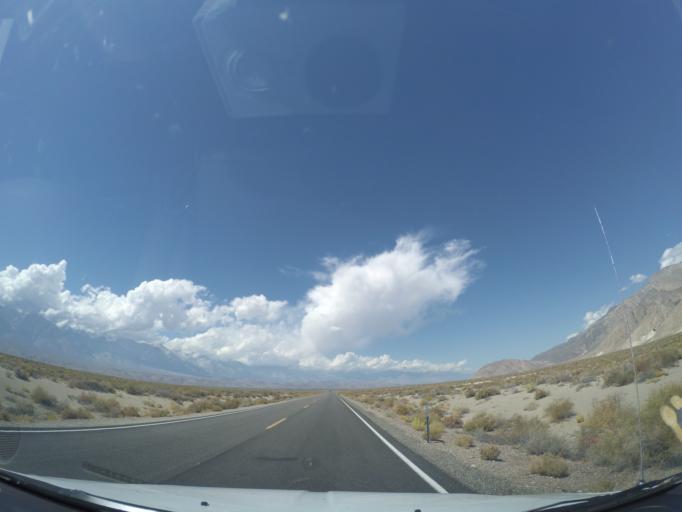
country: US
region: California
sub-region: Inyo County
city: Lone Pine
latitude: 36.5568
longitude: -117.9619
